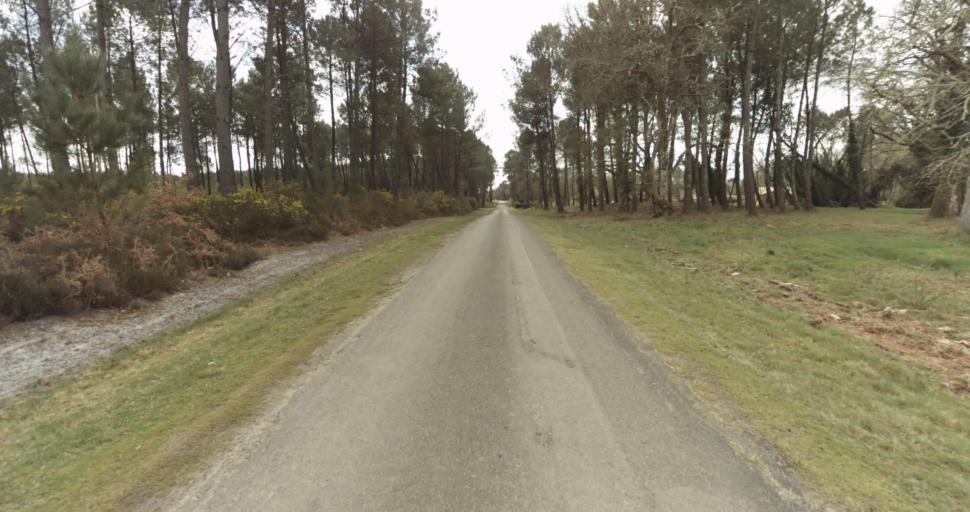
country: FR
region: Aquitaine
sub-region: Departement des Landes
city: Roquefort
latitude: 44.0588
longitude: -0.4300
